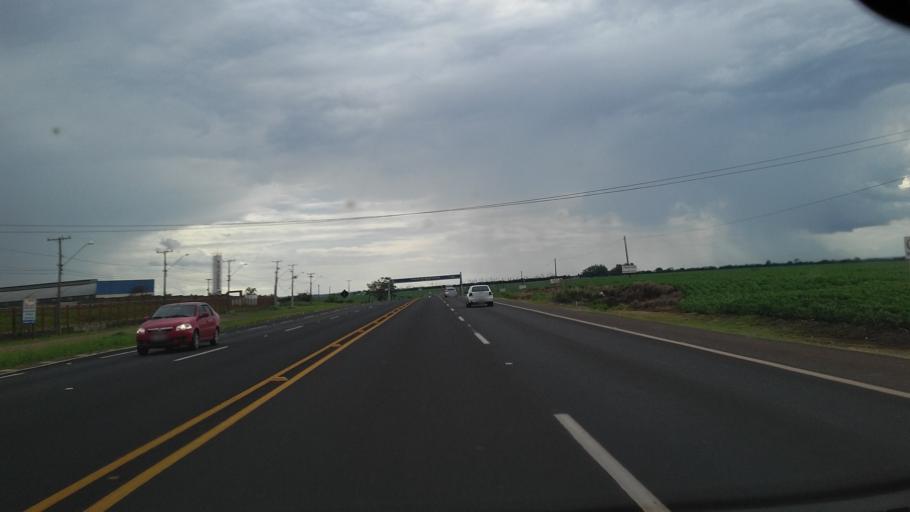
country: BR
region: Parana
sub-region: Arapongas
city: Arapongas
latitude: -23.4107
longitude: -51.4692
